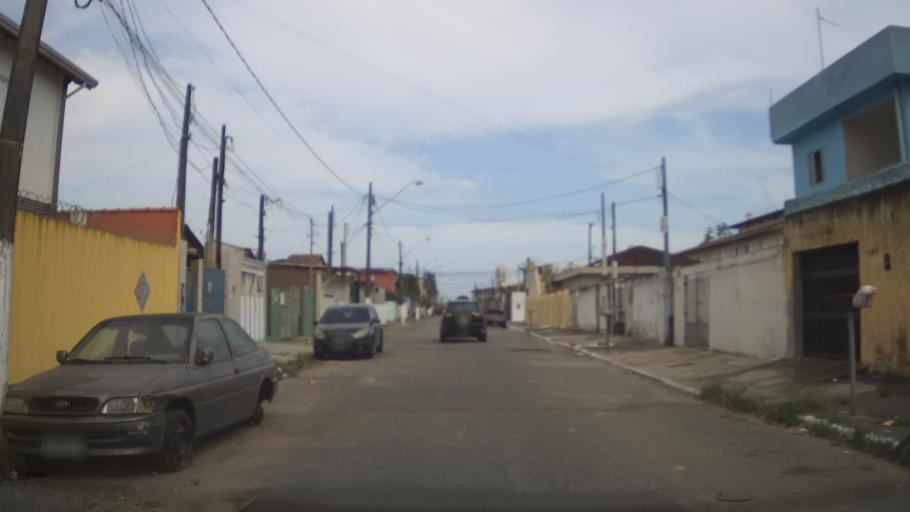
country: BR
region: Sao Paulo
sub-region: Praia Grande
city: Praia Grande
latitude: -24.0056
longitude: -46.4413
